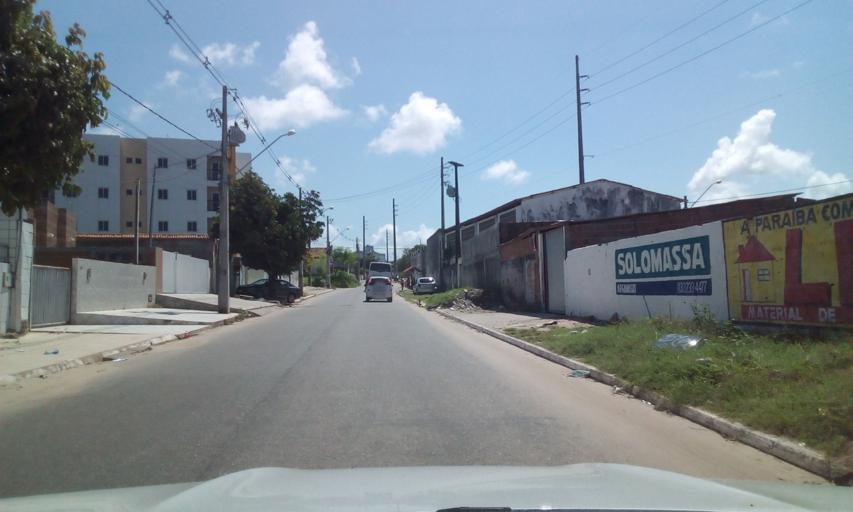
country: BR
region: Paraiba
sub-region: Conde
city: Conde
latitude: -7.2075
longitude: -34.8519
